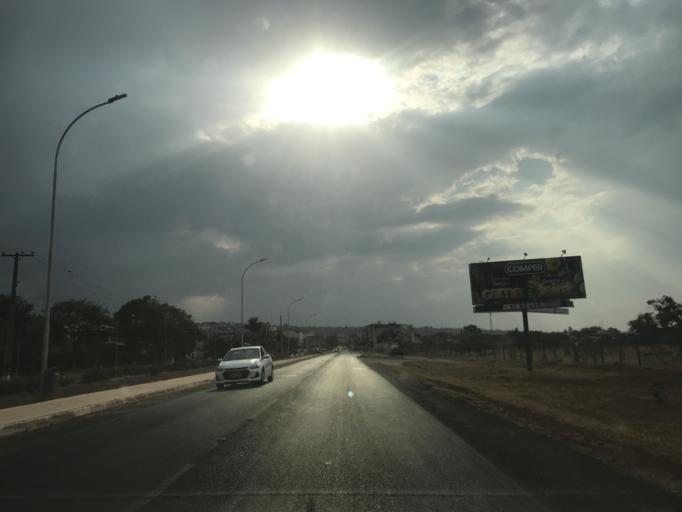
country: BR
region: Federal District
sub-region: Brasilia
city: Brasilia
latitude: -15.6626
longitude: -47.8313
